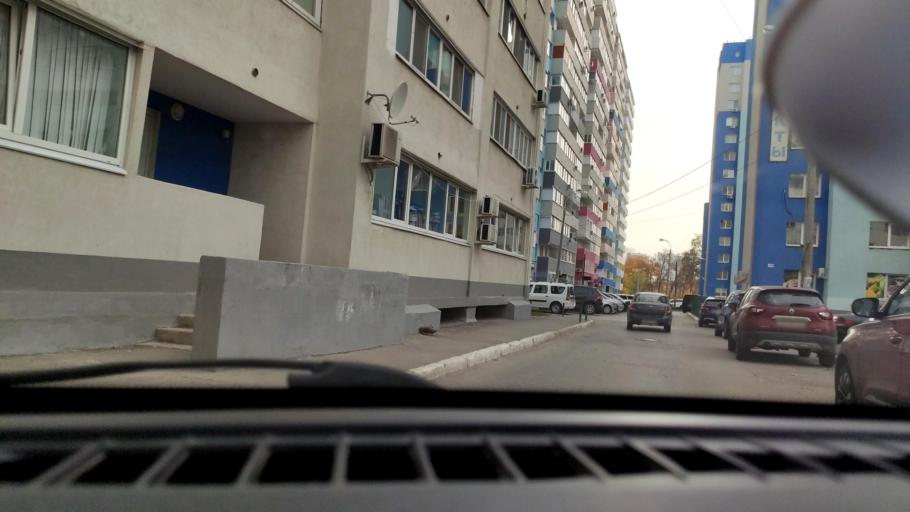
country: RU
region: Samara
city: Petra-Dubrava
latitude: 53.2770
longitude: 50.2626
